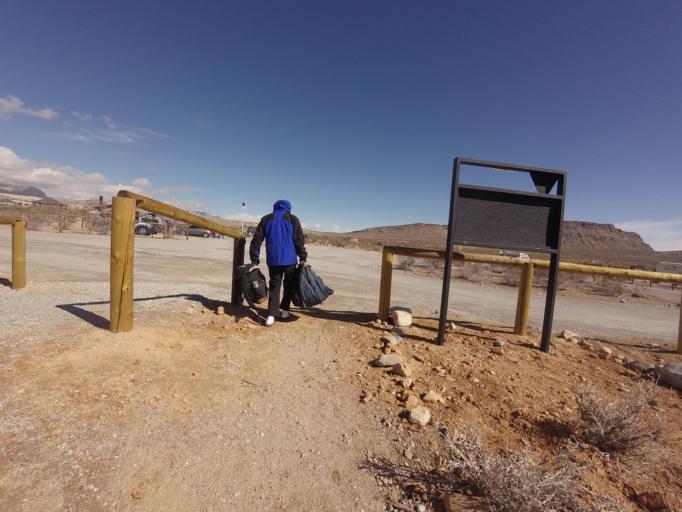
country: US
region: Nevada
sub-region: Clark County
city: Summerlin South
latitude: 36.1293
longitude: -115.3848
